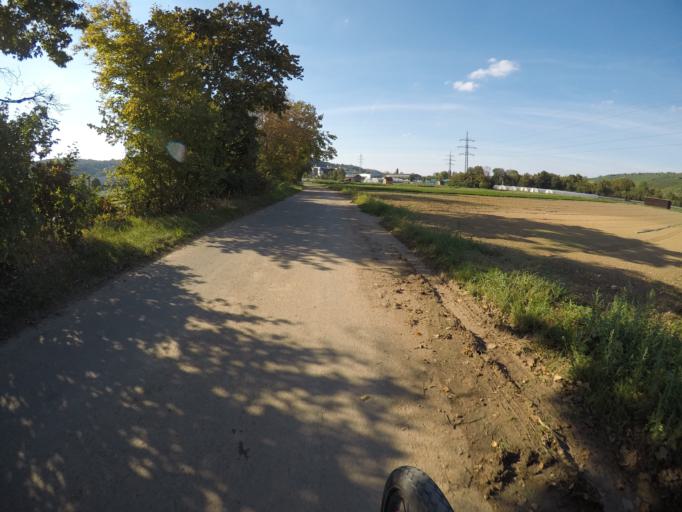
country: DE
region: Baden-Wuerttemberg
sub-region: Regierungsbezirk Stuttgart
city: Esslingen
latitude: 48.7386
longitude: 9.2802
